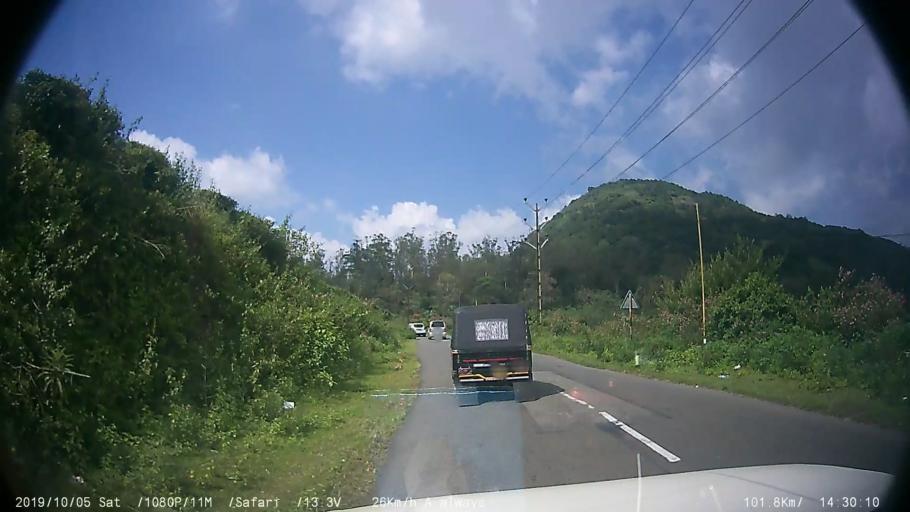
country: IN
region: Kerala
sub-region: Kottayam
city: Erattupetta
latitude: 9.6096
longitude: 76.9690
